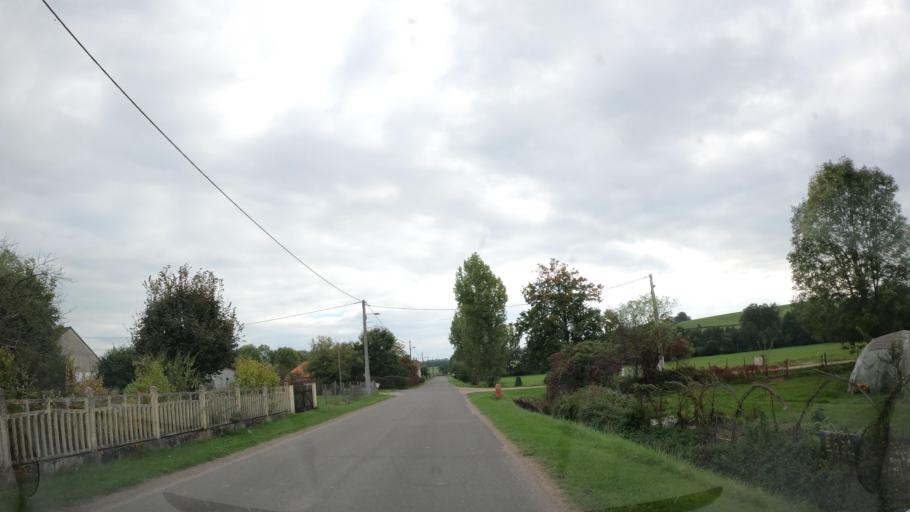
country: FR
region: Auvergne
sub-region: Departement de l'Allier
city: Lapalisse
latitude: 46.3251
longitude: 3.6298
